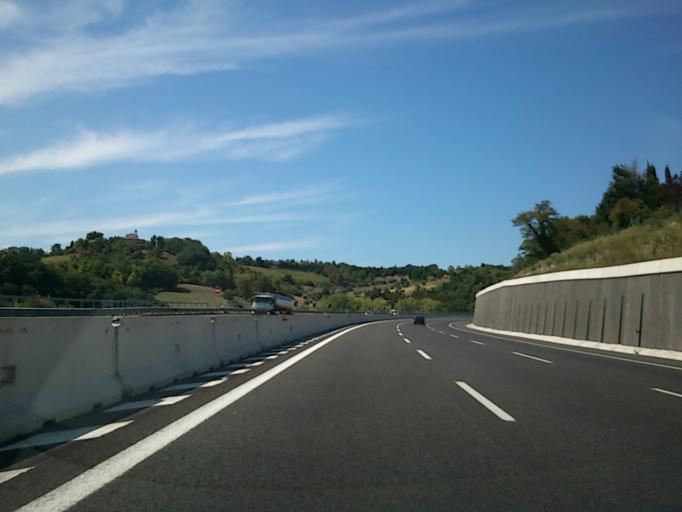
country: IT
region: The Marches
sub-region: Provincia di Pesaro e Urbino
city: Fenile
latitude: 43.8520
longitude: 12.9530
